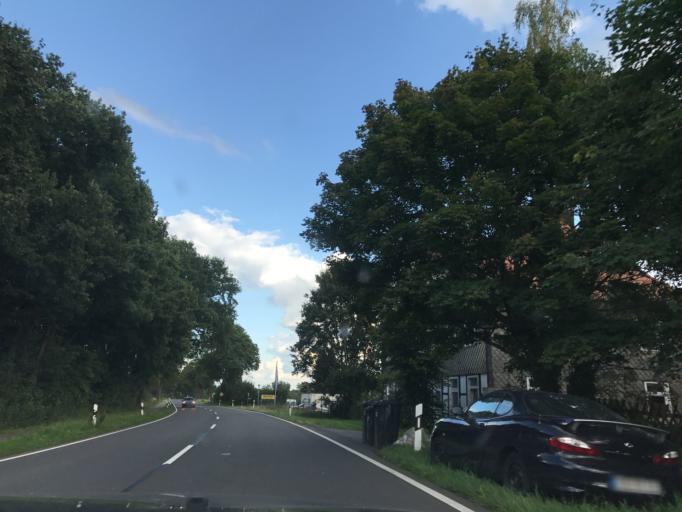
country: DE
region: Lower Saxony
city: Klein Schwulper
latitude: 52.3269
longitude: 10.4353
